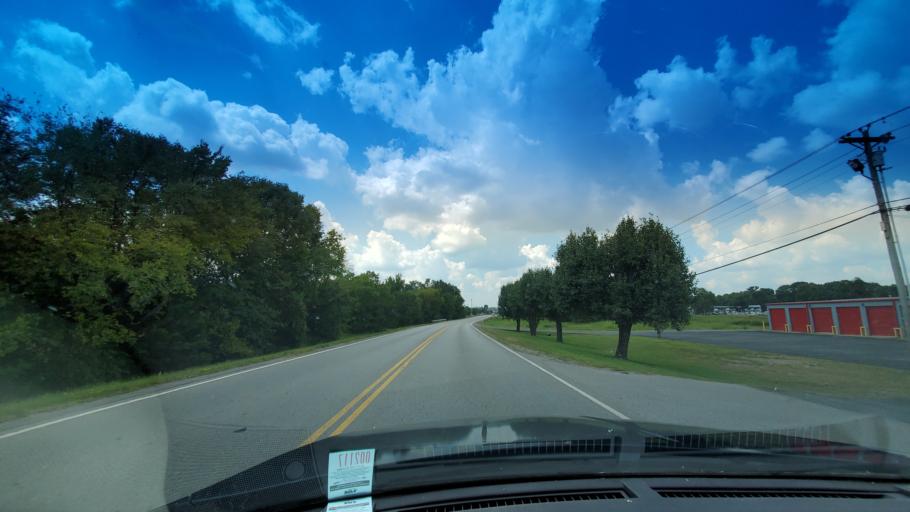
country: US
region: Tennessee
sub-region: Wilson County
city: Lebanon
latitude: 36.1730
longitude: -86.2951
